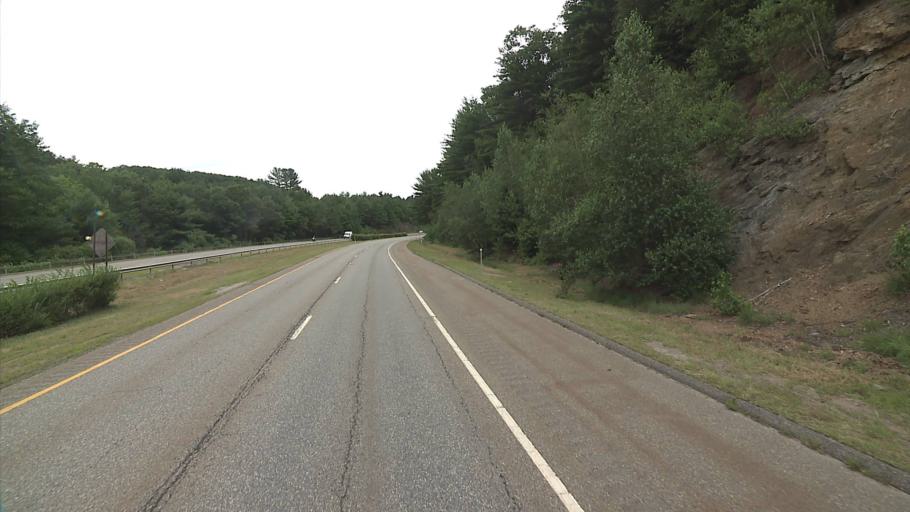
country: US
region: Connecticut
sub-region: Litchfield County
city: Northwest Harwinton
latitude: 41.7545
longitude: -73.1137
